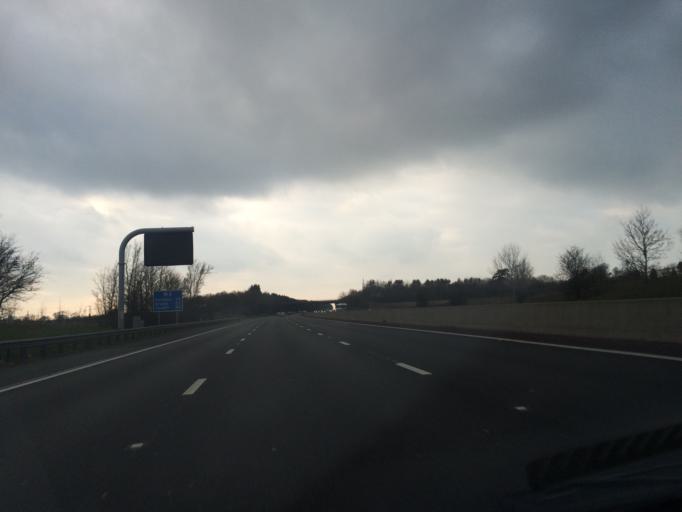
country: GB
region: England
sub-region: West Berkshire
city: Hungerford
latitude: 51.4579
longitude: -1.4973
